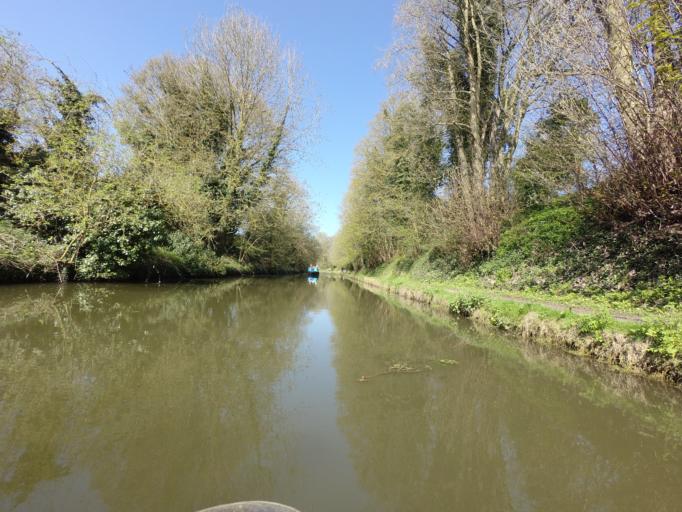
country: GB
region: England
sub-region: Hertfordshire
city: Tring
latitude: 51.7950
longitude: -0.6209
